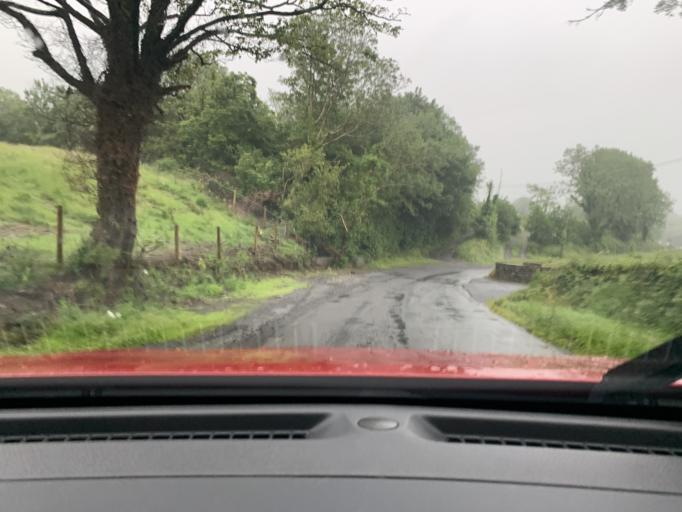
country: IE
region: Connaught
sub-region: Sligo
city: Sligo
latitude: 54.3257
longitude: -8.4229
